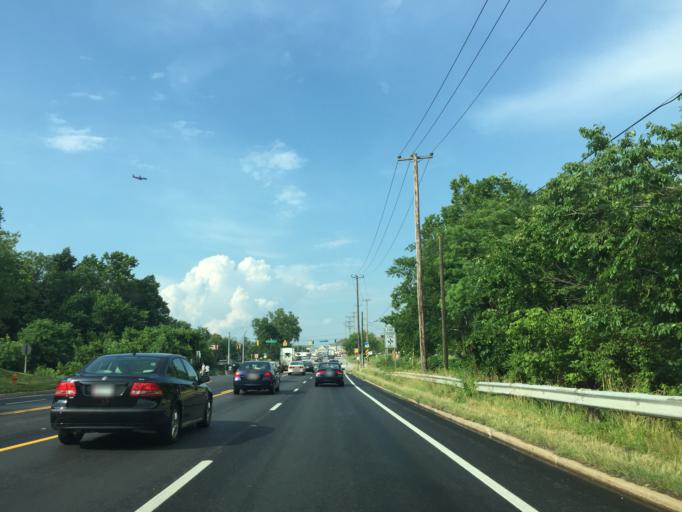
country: US
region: Maryland
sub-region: Anne Arundel County
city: Jessup
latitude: 39.1683
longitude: -76.7885
